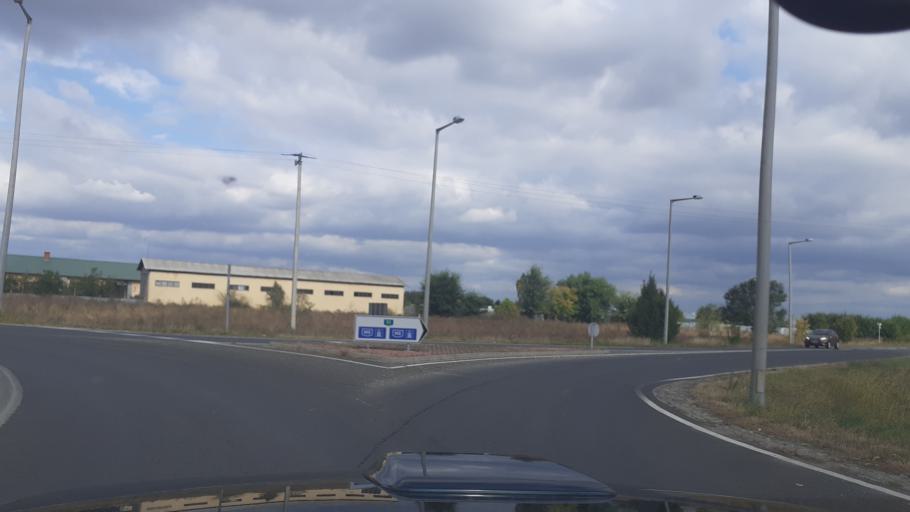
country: HU
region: Bacs-Kiskun
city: Dunavecse
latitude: 46.8993
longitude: 18.9761
